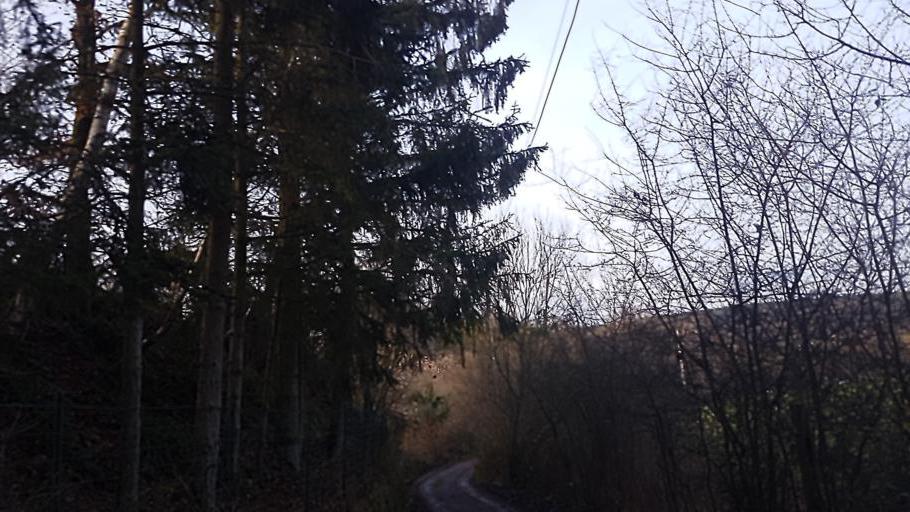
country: FR
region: Champagne-Ardenne
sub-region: Departement des Ardennes
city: Vireux-Molhain
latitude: 50.0681
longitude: 4.6136
